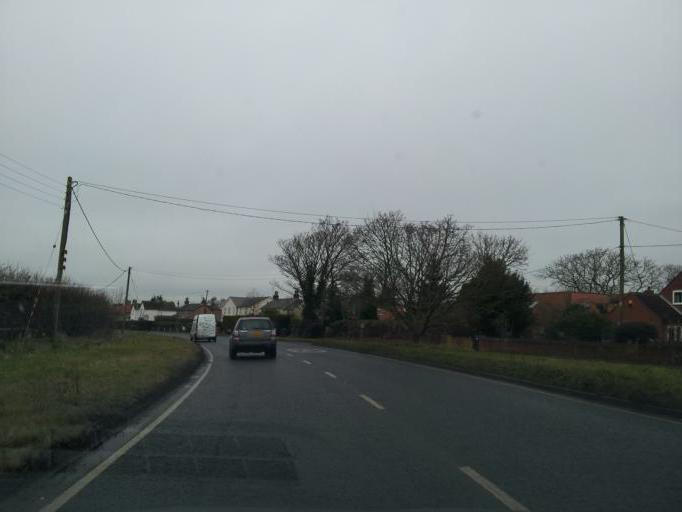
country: GB
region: England
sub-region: Essex
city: Manningtree
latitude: 51.9692
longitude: 1.0742
